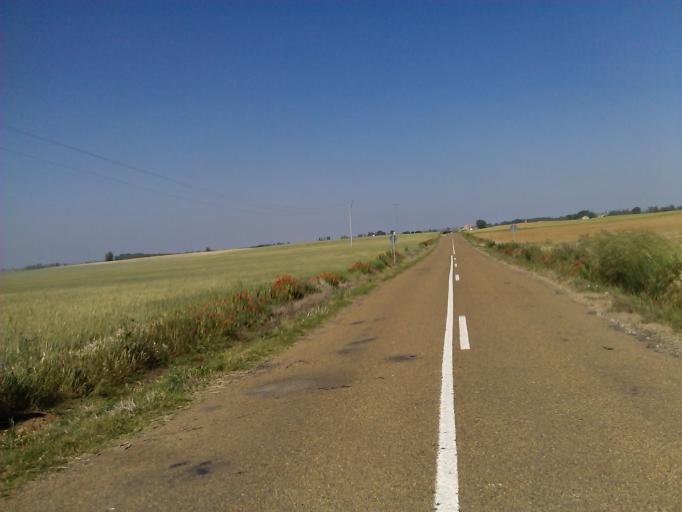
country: ES
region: Castille and Leon
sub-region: Provincia de Palencia
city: Boadilla del Camino
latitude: 42.2593
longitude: -4.3214
